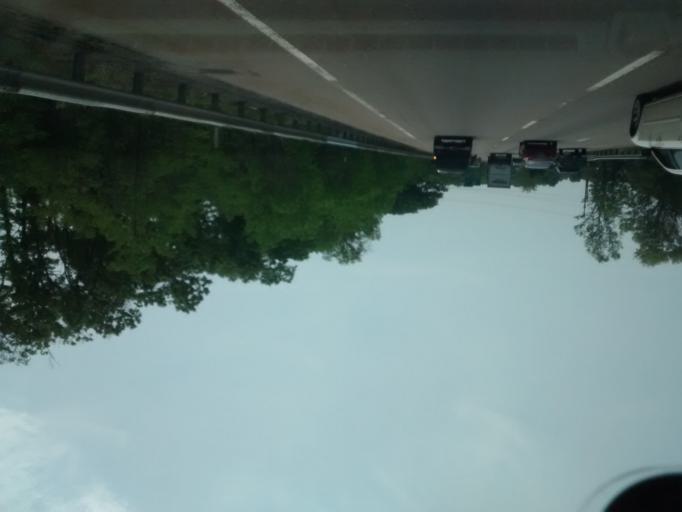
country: US
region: Massachusetts
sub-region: Norfolk County
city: Wrentham
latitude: 42.0410
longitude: -71.3505
